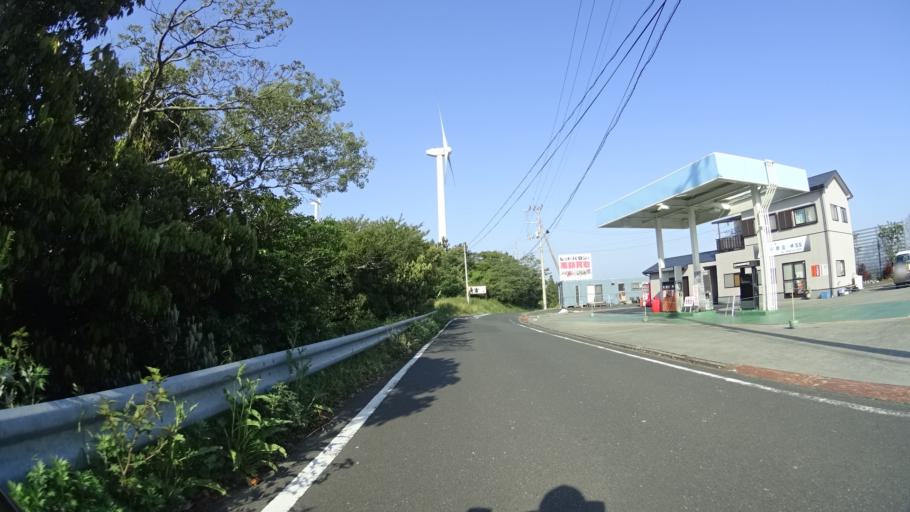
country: JP
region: Ehime
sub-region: Nishiuwa-gun
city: Ikata-cho
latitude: 33.3824
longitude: 132.0761
